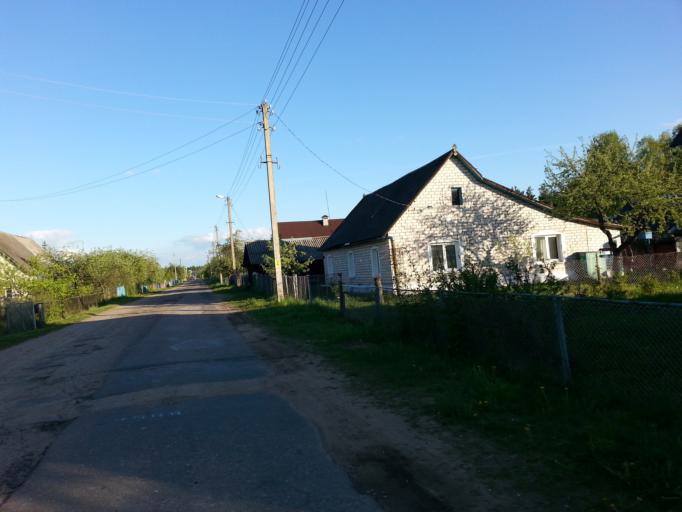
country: BY
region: Minsk
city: Narach
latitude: 54.9322
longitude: 26.6787
